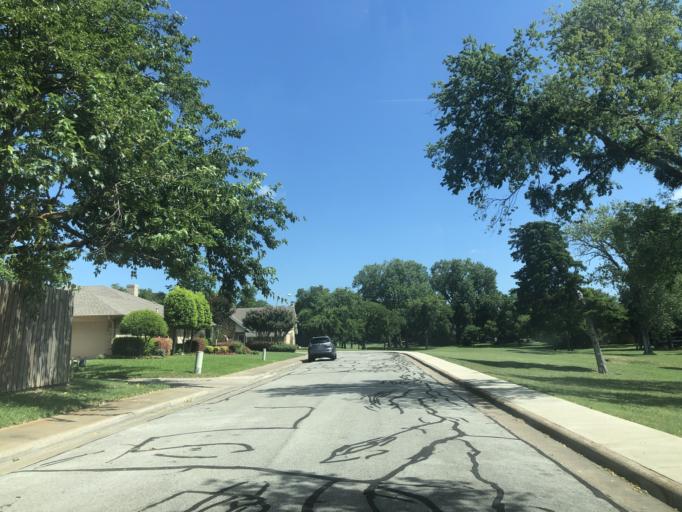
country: US
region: Texas
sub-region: Dallas County
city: Duncanville
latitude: 32.6489
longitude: -96.9300
